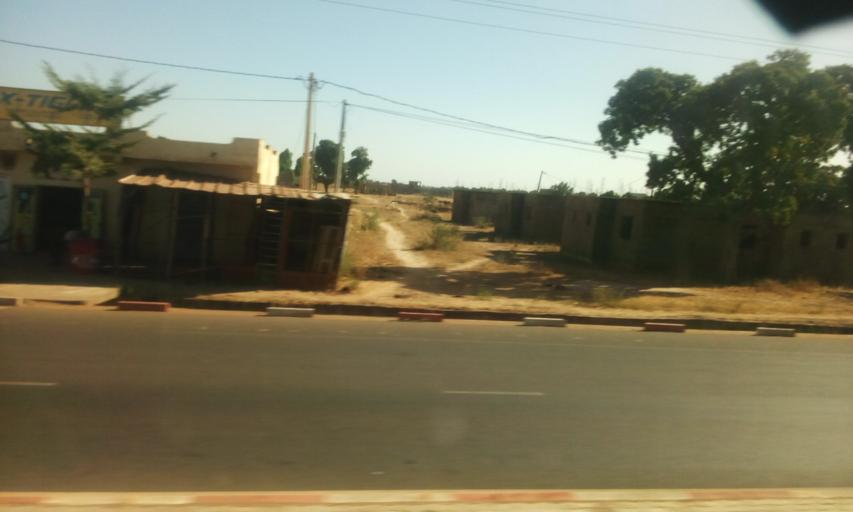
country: ML
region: Segou
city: Segou
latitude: 13.4214
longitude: -6.2949
